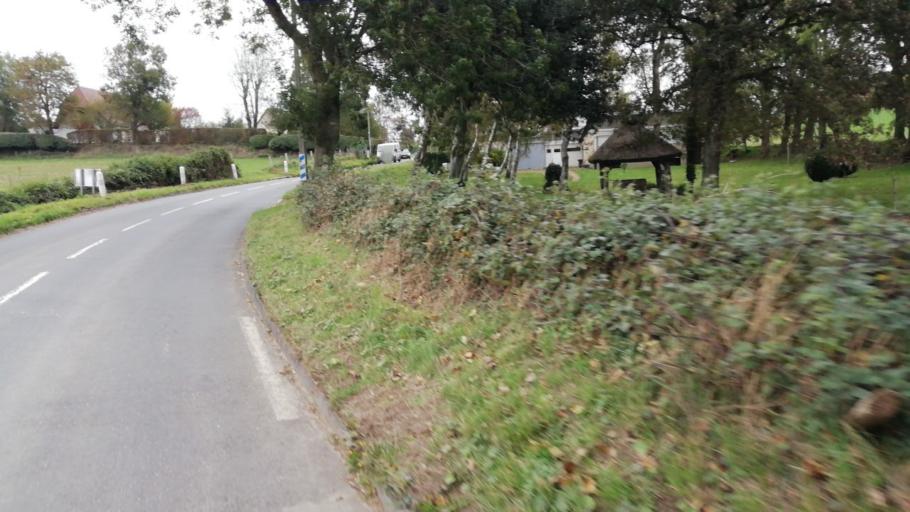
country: FR
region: Haute-Normandie
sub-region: Departement de la Seine-Maritime
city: Fontaine-la-Mallet
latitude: 49.5445
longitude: 0.1441
